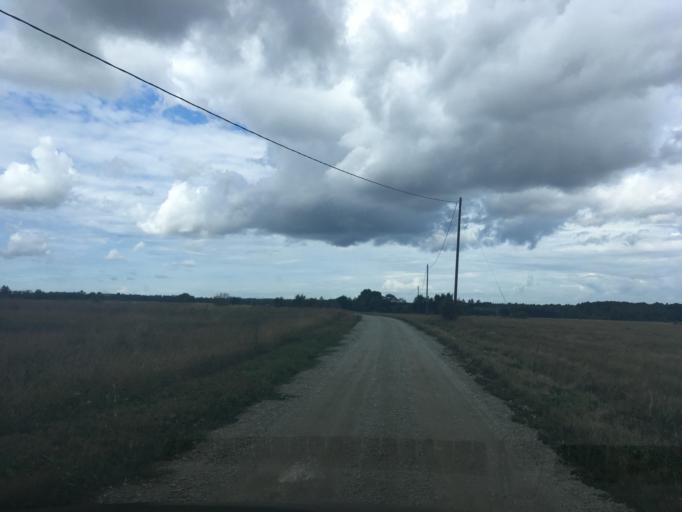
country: EE
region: Harju
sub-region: Rae vald
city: Jueri
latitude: 59.3819
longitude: 24.8869
